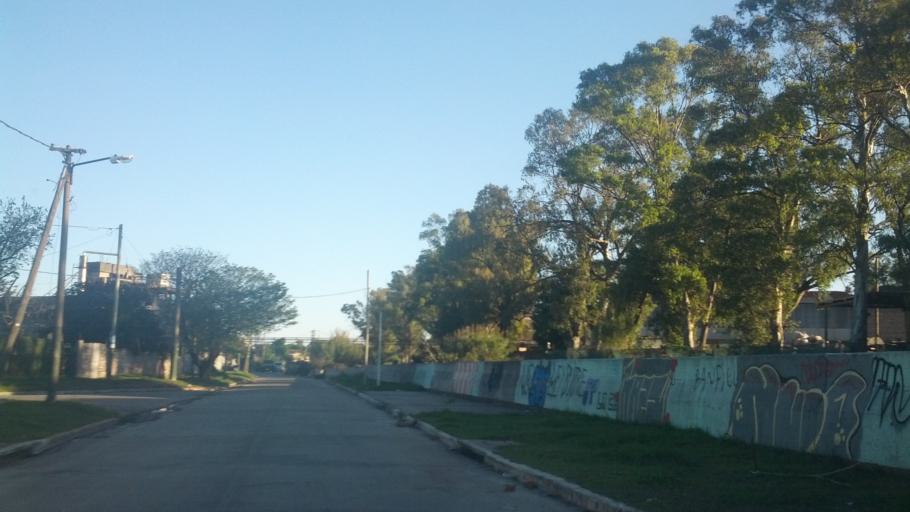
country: AR
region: Buenos Aires
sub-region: Partido de Lomas de Zamora
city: Lomas de Zamora
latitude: -34.7617
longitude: -58.4293
